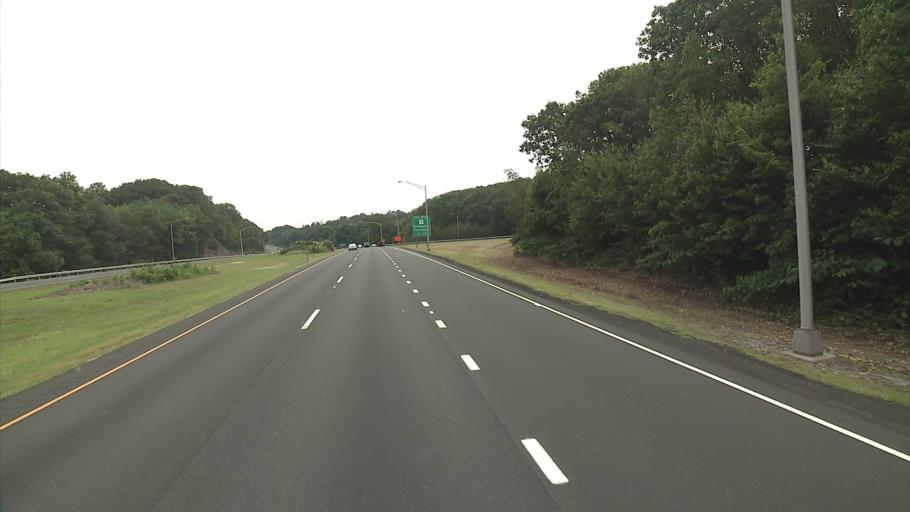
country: US
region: Connecticut
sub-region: New Haven County
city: Waterbury
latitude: 41.5408
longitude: -73.0794
